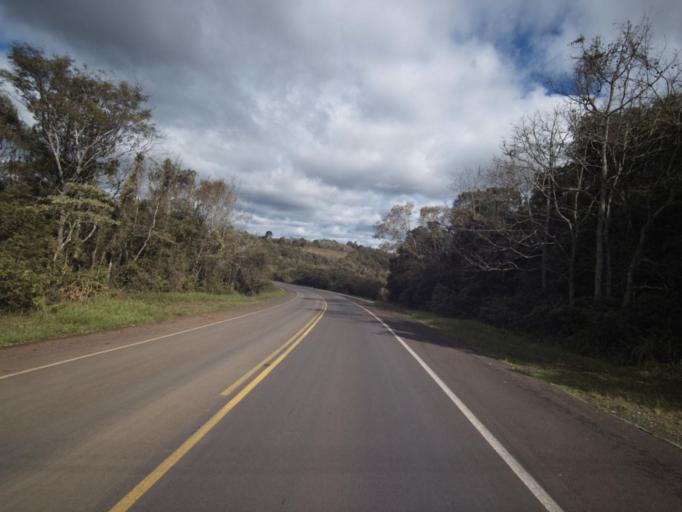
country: BR
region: Santa Catarina
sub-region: Concordia
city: Concordia
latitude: -27.3394
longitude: -51.9837
